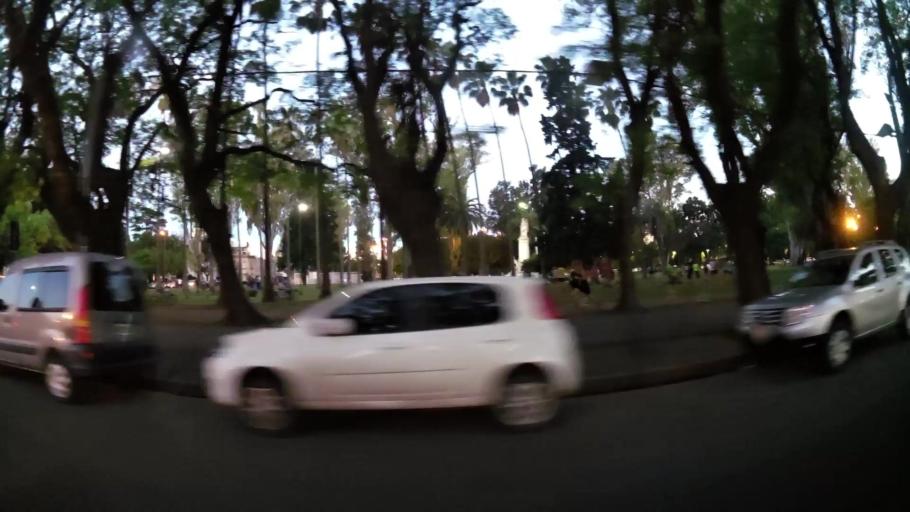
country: AR
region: Santa Fe
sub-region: Departamento de Rosario
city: Rosario
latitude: -32.9561
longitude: -60.6563
